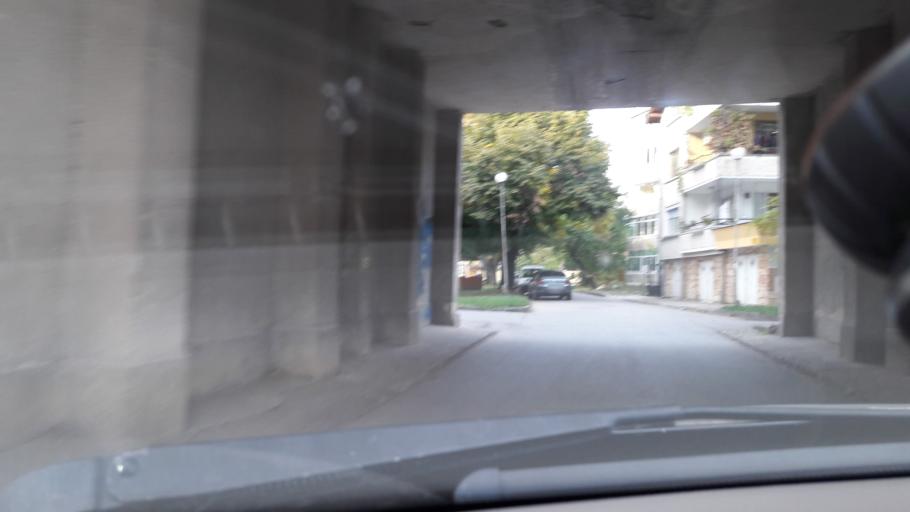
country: BG
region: Razgrad
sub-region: Obshtina Razgrad
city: Razgrad
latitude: 43.5290
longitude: 26.5251
